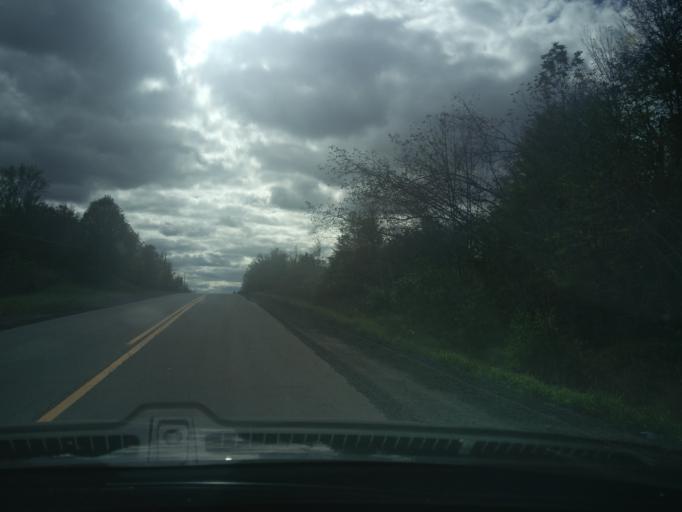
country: CA
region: Ontario
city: Perth
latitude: 44.7378
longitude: -76.3926
